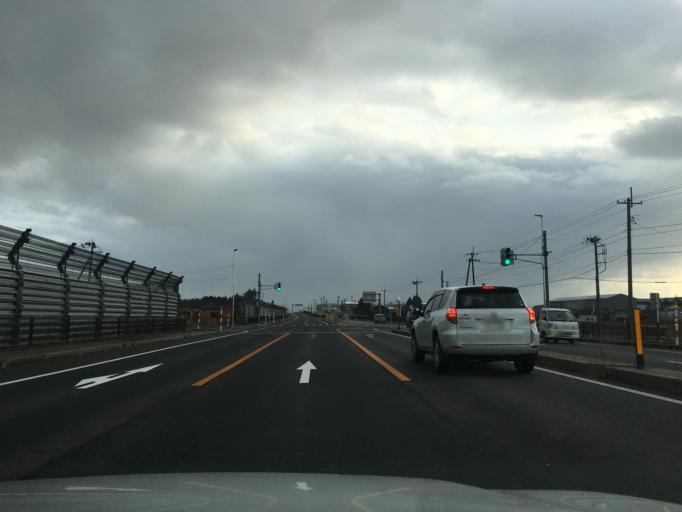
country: JP
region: Yamagata
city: Tsuruoka
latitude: 38.7185
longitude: 139.7615
